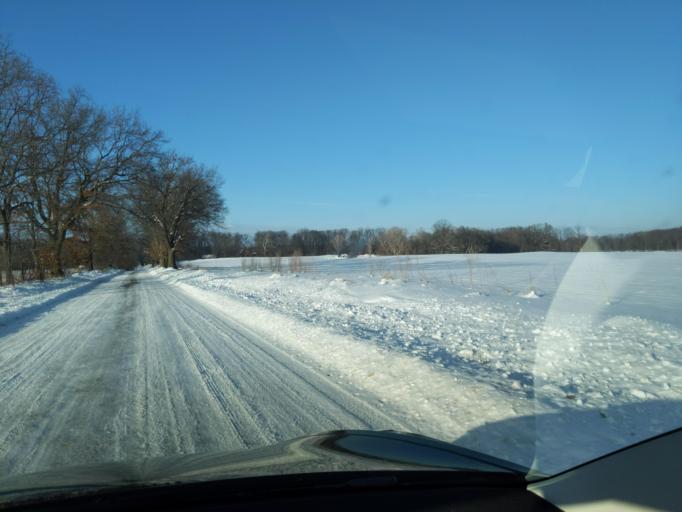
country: US
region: Michigan
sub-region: Ingham County
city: Stockbridge
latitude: 42.4565
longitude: -84.1185
